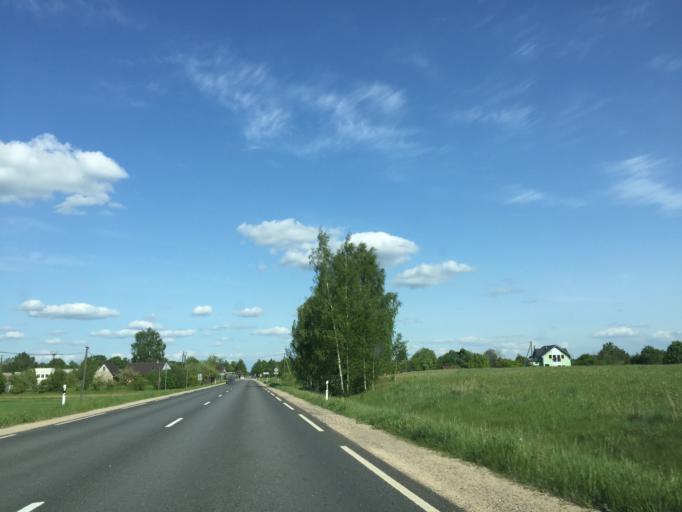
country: LV
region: Salaspils
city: Salaspils
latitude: 56.8217
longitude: 24.4075
